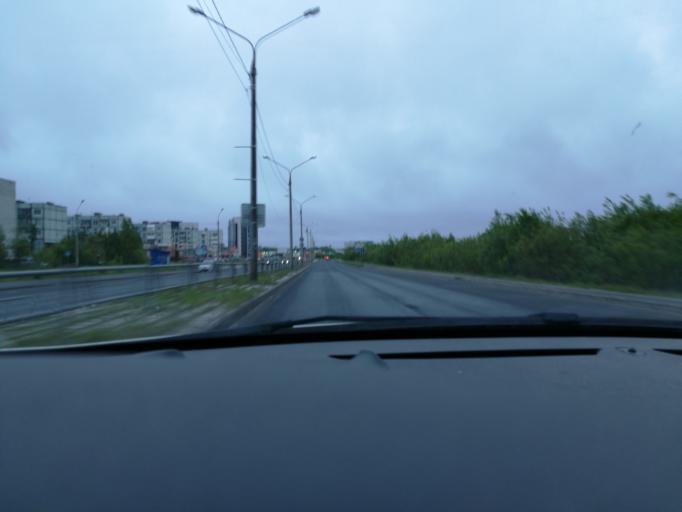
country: RU
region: Arkhangelskaya
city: Severodvinsk
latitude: 64.5625
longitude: 39.7815
